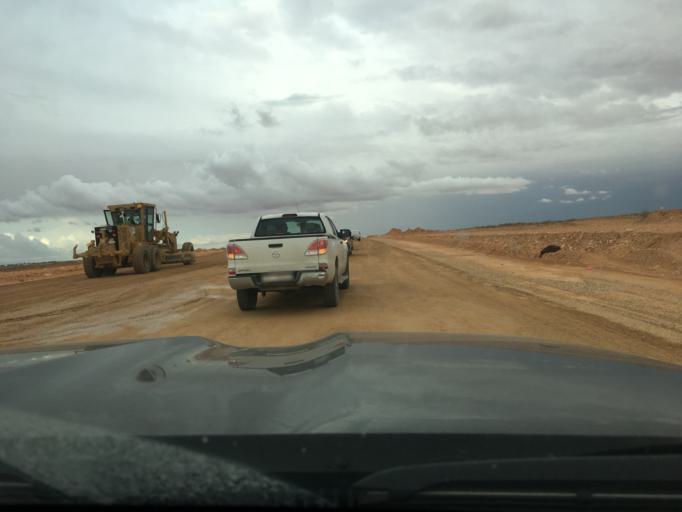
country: TN
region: Madanin
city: Medenine
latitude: 33.2636
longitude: 10.5798
